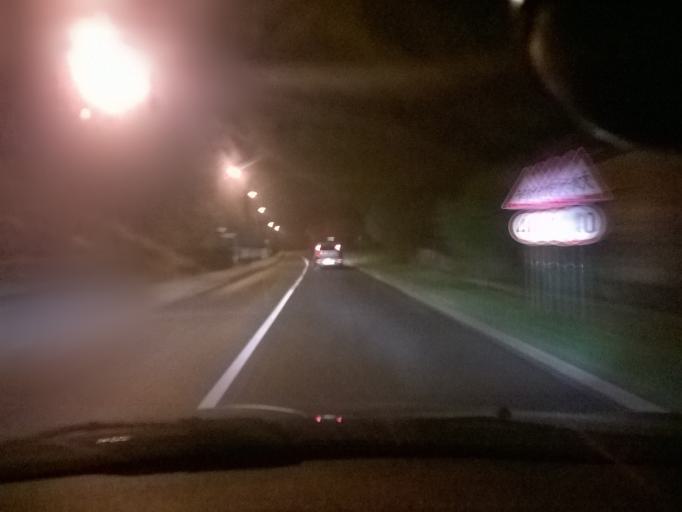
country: HR
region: Krapinsko-Zagorska
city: Zabok
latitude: 46.0339
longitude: 15.9107
